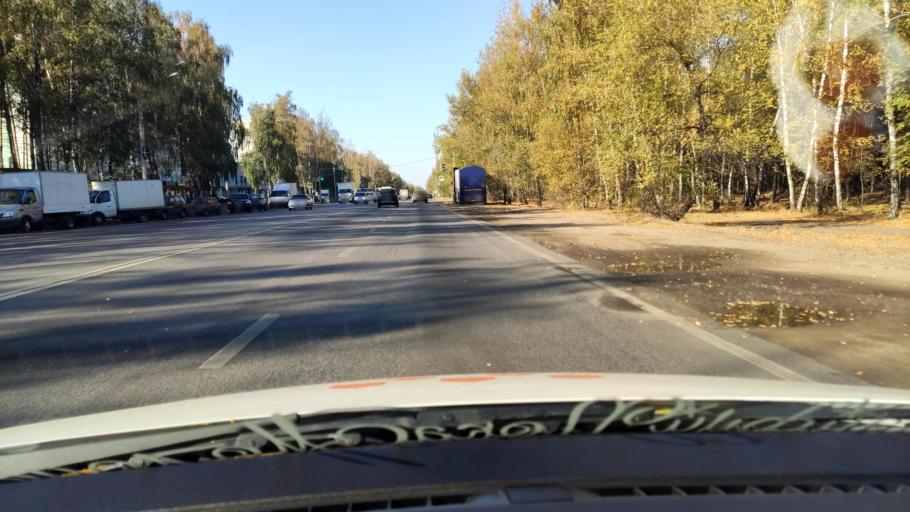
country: RU
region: Voronezj
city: Pridonskoy
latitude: 51.6866
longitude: 39.1113
